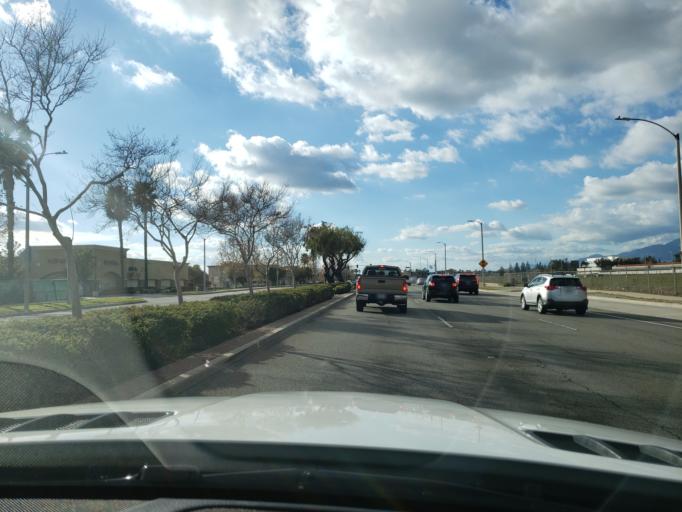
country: US
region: California
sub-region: San Bernardino County
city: Rancho Cucamonga
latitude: 34.1064
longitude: -117.5504
